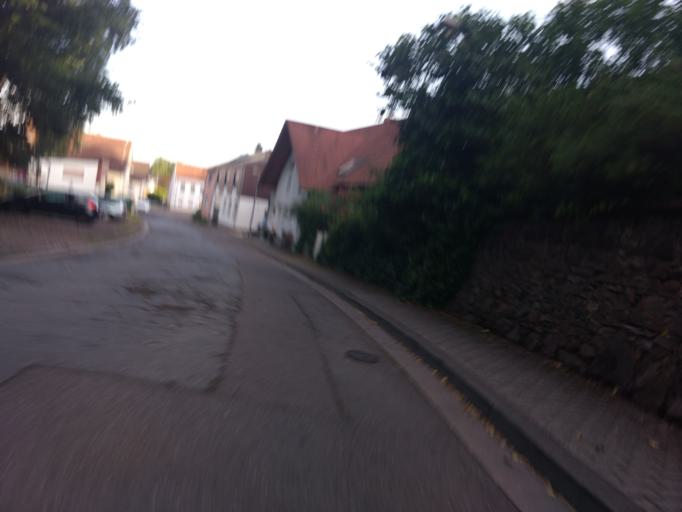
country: DE
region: Saarland
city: Wallerfangen
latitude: 49.3205
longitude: 6.7255
